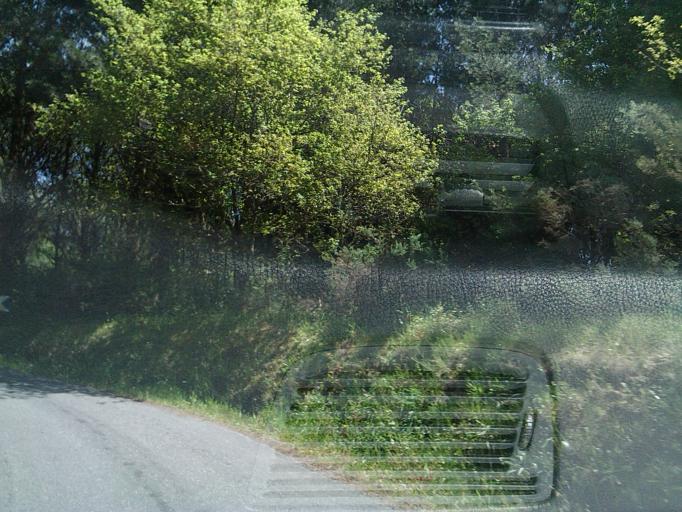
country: ES
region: Galicia
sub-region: Provincia de Lugo
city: Guitiriz
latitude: 43.1617
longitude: -7.8281
